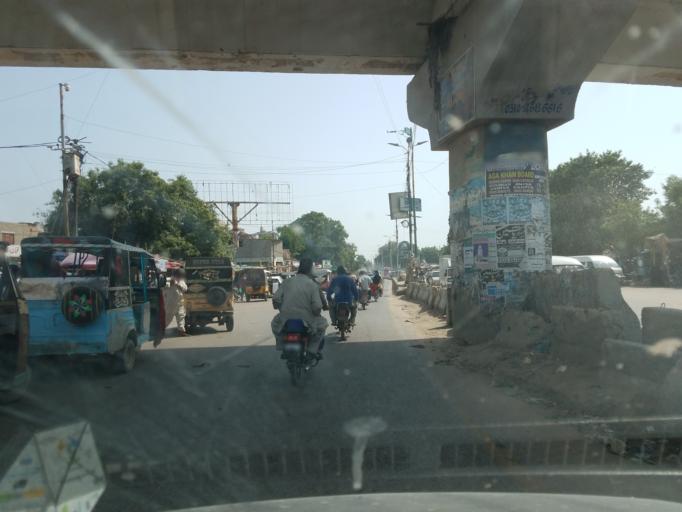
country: PK
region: Sindh
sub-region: Karachi District
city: Karachi
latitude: 24.8922
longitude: 67.0436
